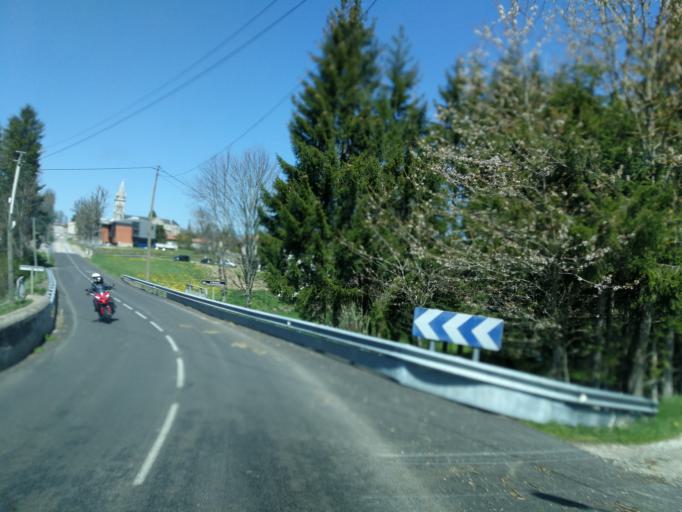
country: FR
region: Rhone-Alpes
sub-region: Departement de la Loire
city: Marlhes
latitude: 45.2789
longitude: 4.3958
